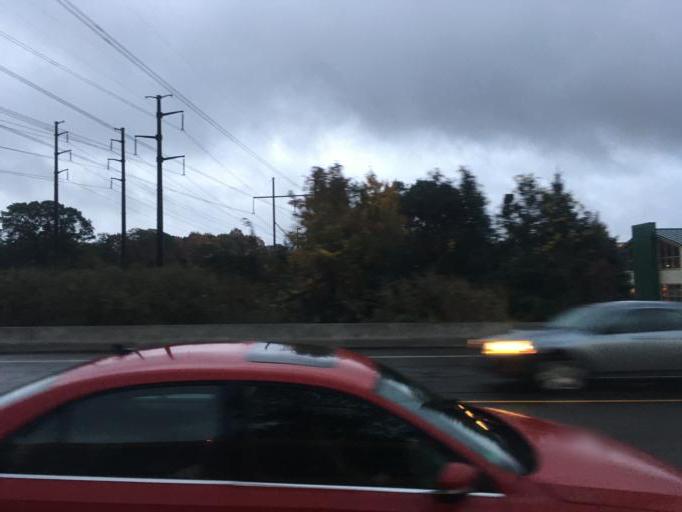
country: US
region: Rhode Island
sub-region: Kent County
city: West Warwick
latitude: 41.7044
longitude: -71.4937
